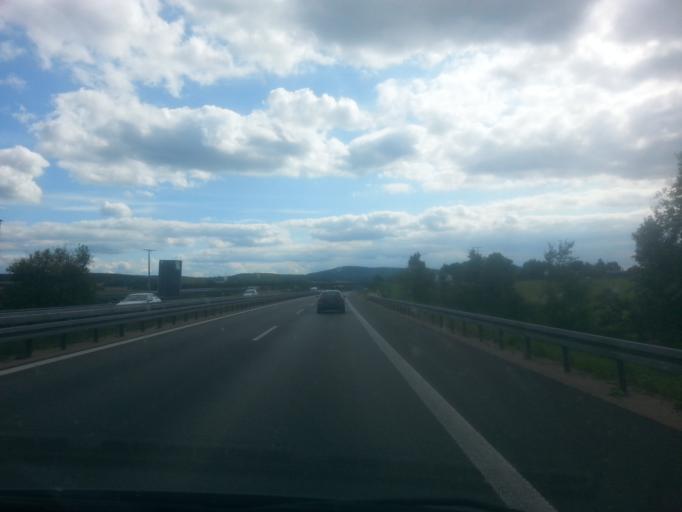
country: DE
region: Bavaria
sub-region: Upper Palatinate
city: Nabburg
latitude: 49.4696
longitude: 12.1941
